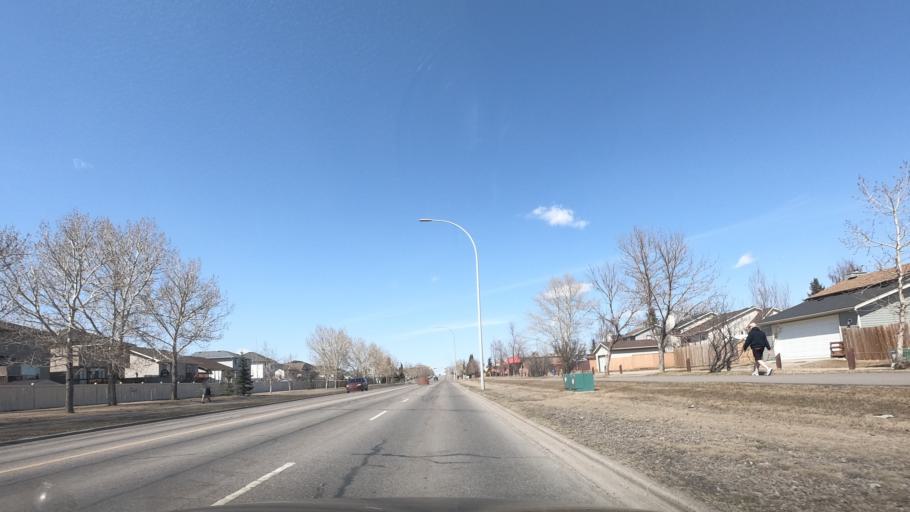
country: CA
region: Alberta
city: Airdrie
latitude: 51.2741
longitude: -113.9898
